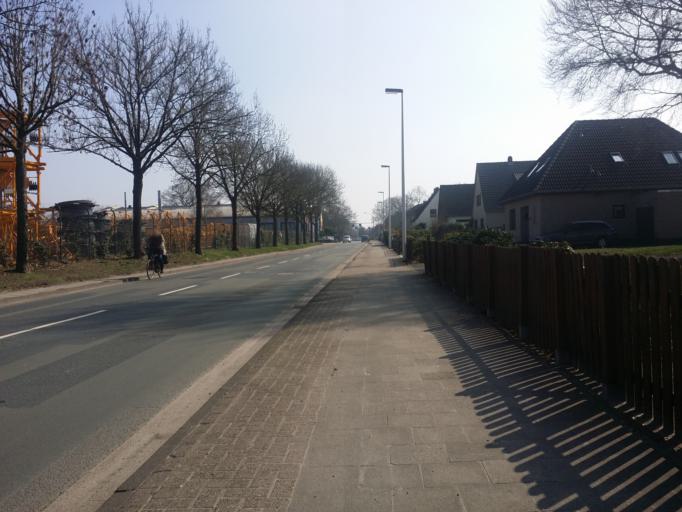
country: DE
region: Lower Saxony
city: Delmenhorst
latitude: 53.0199
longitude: 8.6438
